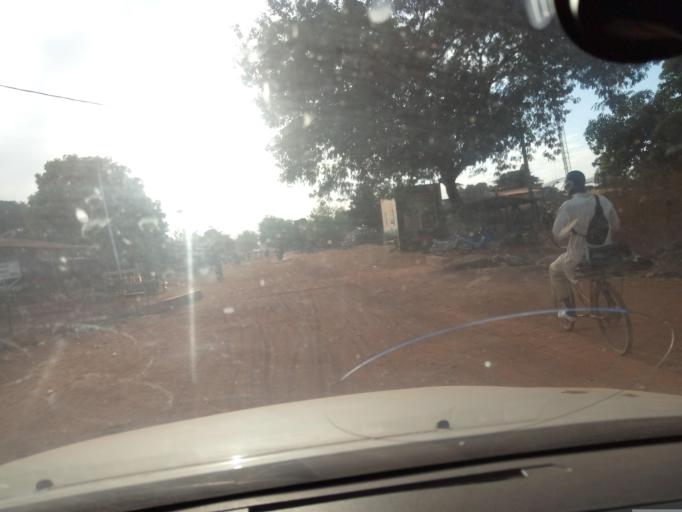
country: ML
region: Sikasso
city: Sikasso
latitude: 11.3155
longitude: -5.6445
